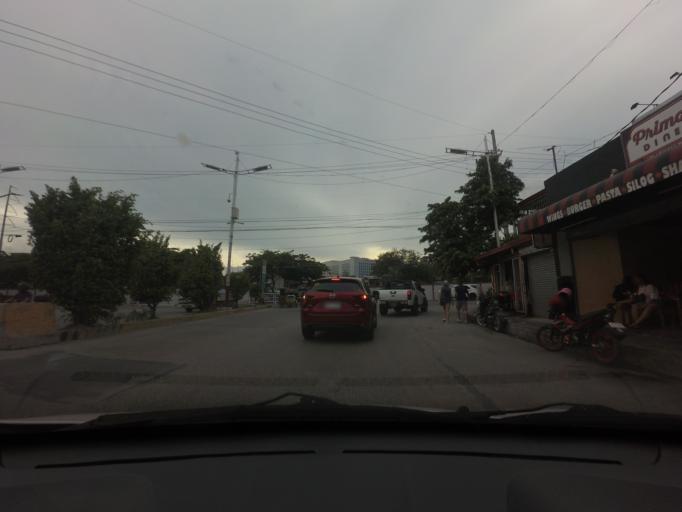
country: PH
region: Calabarzon
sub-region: Province of Rizal
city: Pateros
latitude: 14.5306
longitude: 121.0579
